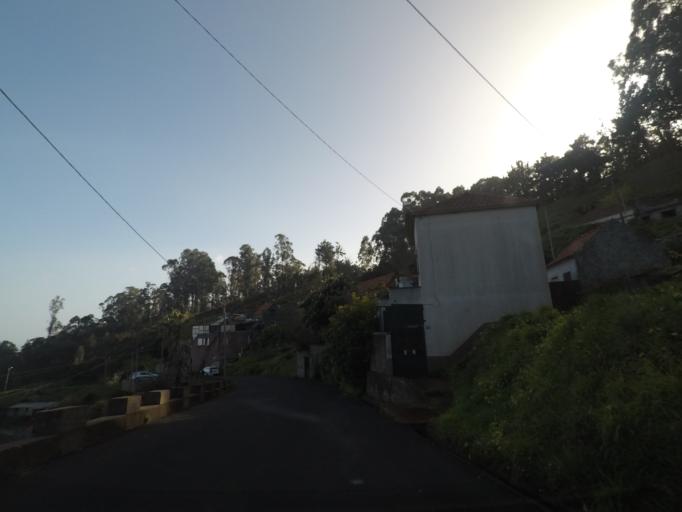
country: PT
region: Madeira
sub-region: Ribeira Brava
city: Campanario
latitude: 32.6791
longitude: -17.0090
